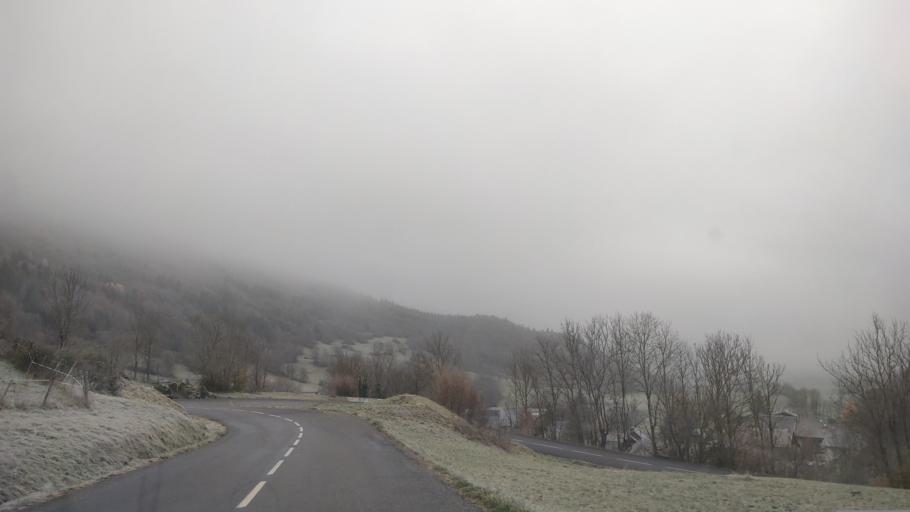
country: FR
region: Rhone-Alpes
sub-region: Departement de la Savoie
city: Coise-Saint-Jean-Pied-Gauthier
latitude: 45.5932
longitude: 6.1376
